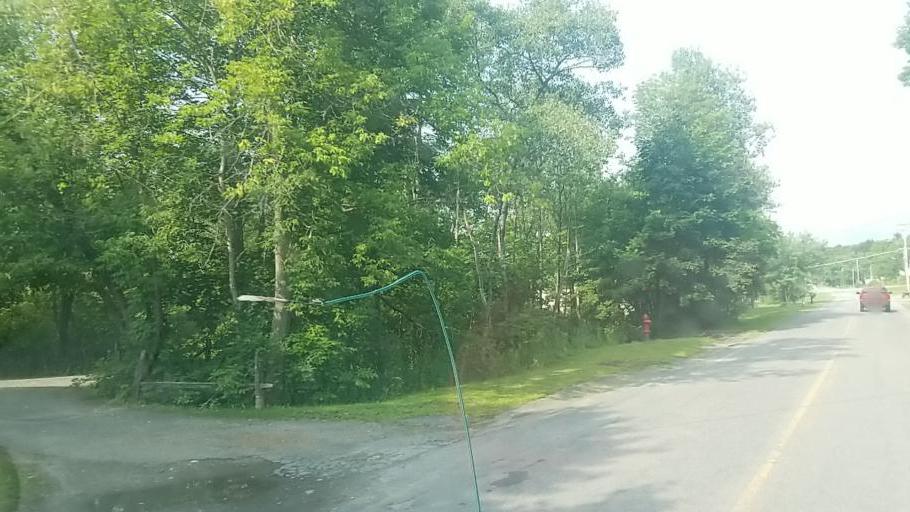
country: US
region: New York
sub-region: Fulton County
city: Broadalbin
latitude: 43.1045
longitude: -74.2699
